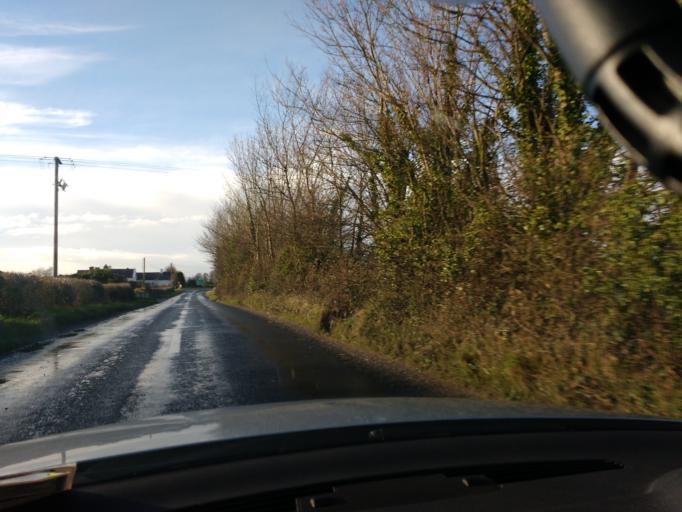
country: IE
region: Munster
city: Thurles
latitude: 52.6320
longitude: -7.7766
